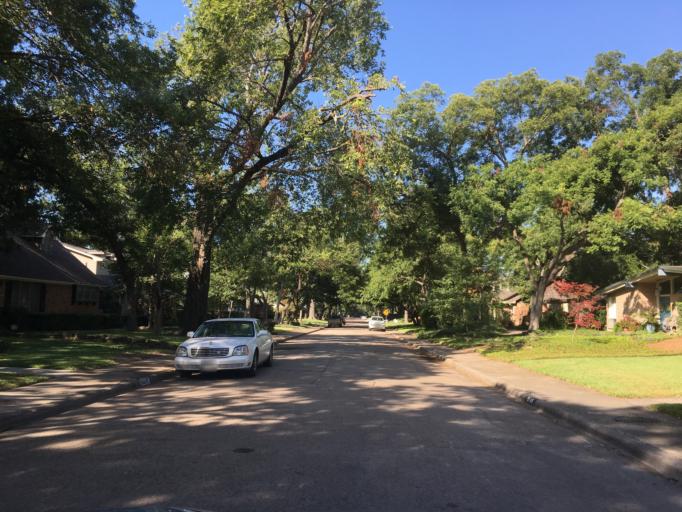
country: US
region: Texas
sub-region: Dallas County
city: Richardson
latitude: 32.8757
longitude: -96.7247
